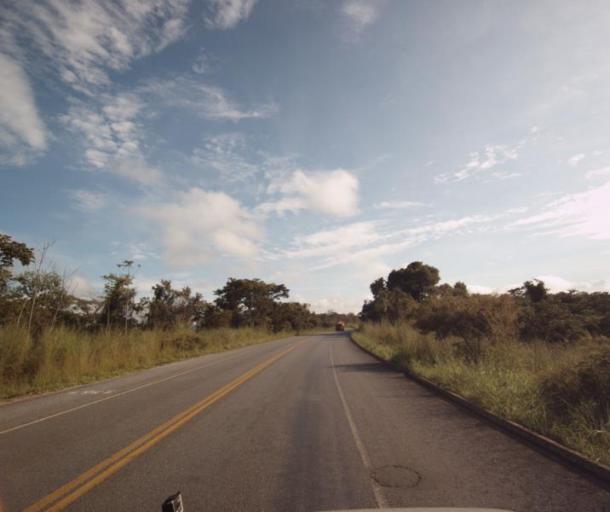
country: BR
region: Goias
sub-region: Pirenopolis
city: Pirenopolis
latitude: -15.5300
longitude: -48.6255
